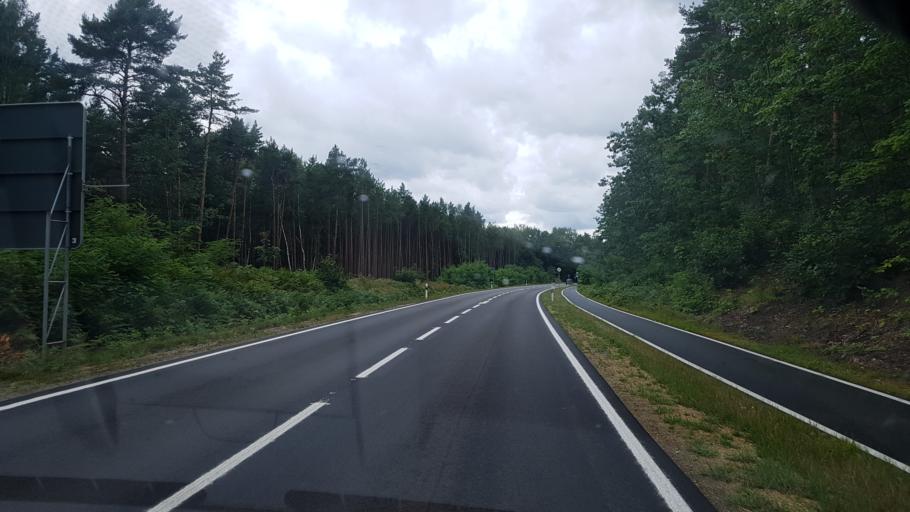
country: DE
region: Saxony
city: Niesky
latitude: 51.2964
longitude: 14.8088
